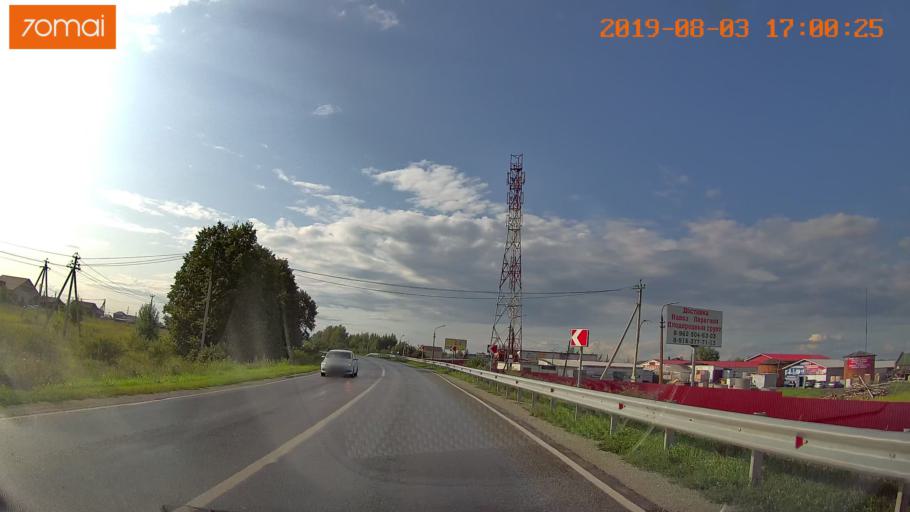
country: RU
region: Moskovskaya
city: Voskresensk
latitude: 55.3371
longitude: 38.6177
